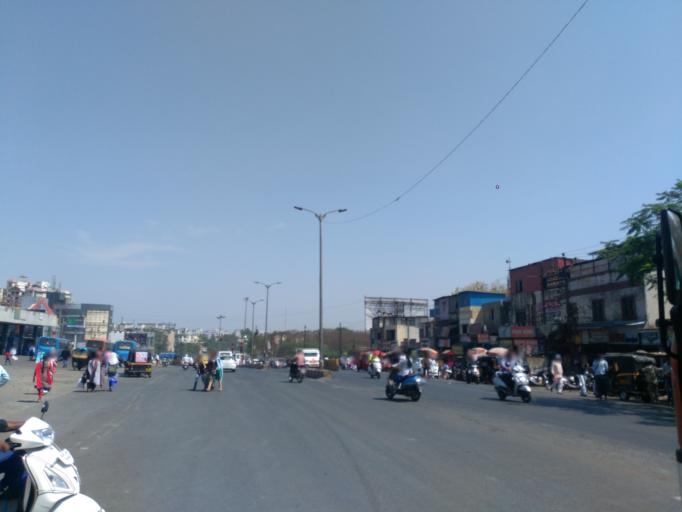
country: IN
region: Maharashtra
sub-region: Pune Division
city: Pune
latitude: 18.4462
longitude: 73.8591
